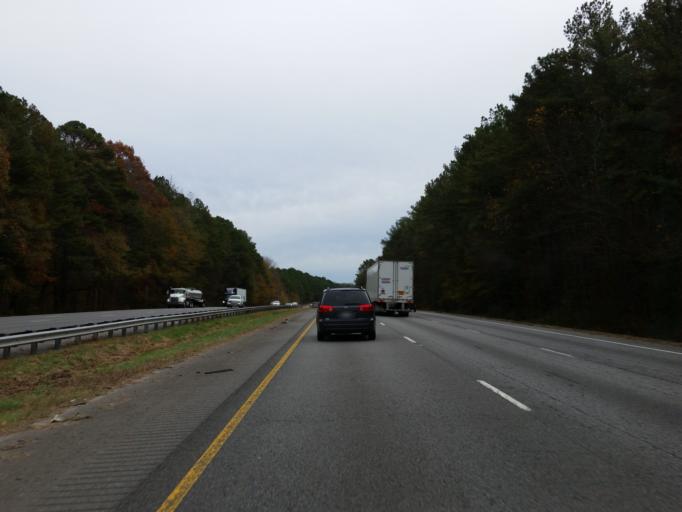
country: US
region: Georgia
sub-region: Butts County
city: Jackson
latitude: 33.1823
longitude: -84.0509
